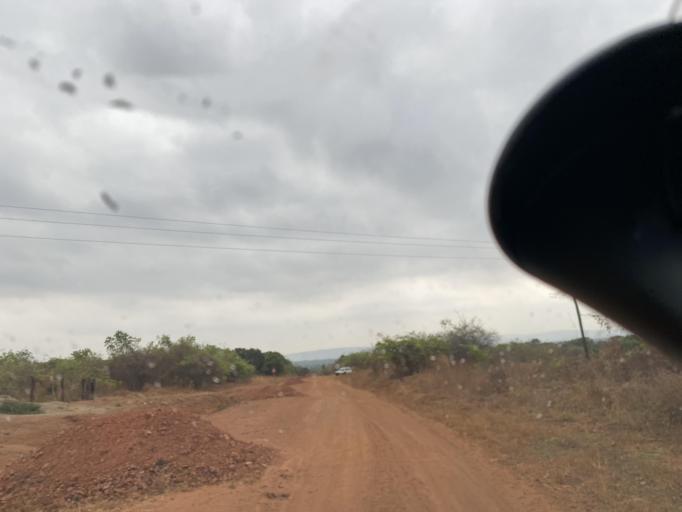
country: ZM
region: Lusaka
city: Chongwe
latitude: -15.1684
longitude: 28.7639
